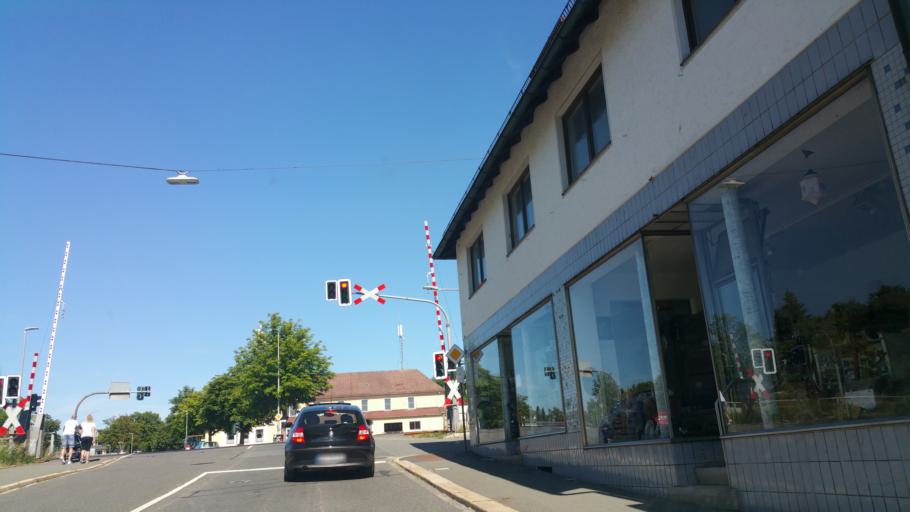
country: DE
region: Bavaria
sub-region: Upper Franconia
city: Rehau
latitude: 50.2491
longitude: 12.0395
